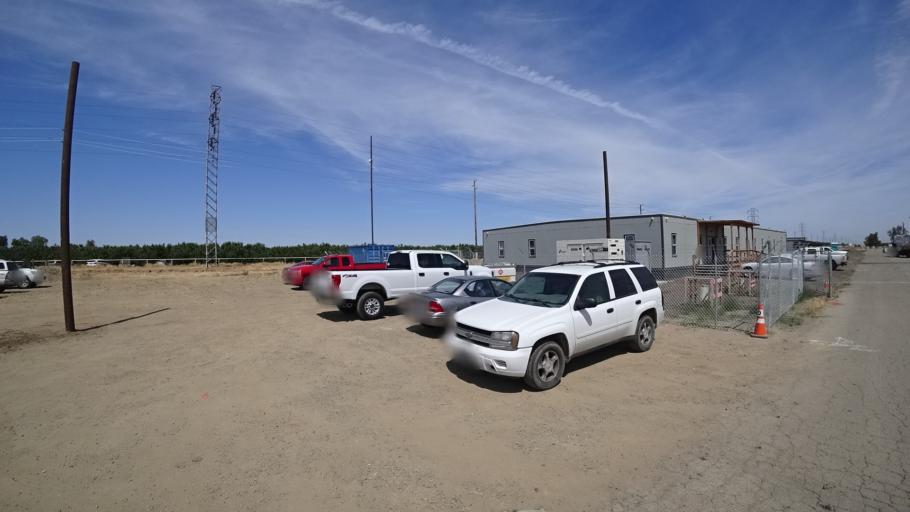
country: US
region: California
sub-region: Kings County
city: Home Garden
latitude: 36.3298
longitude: -119.5914
